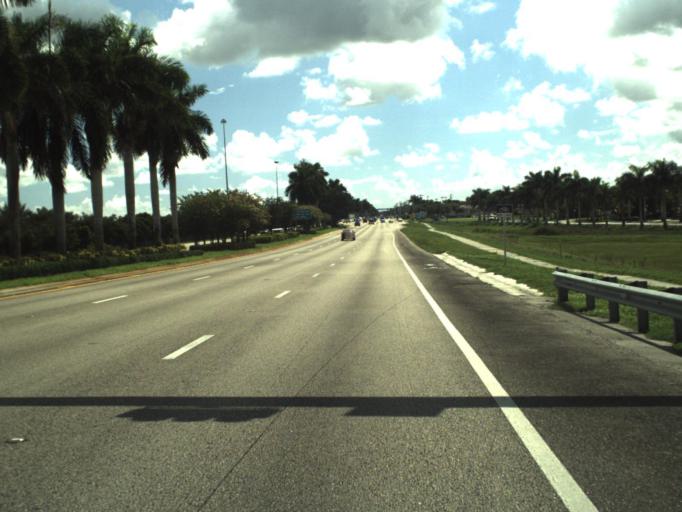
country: US
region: Florida
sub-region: Broward County
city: Sunshine Ranches
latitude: 26.0076
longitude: -80.3379
